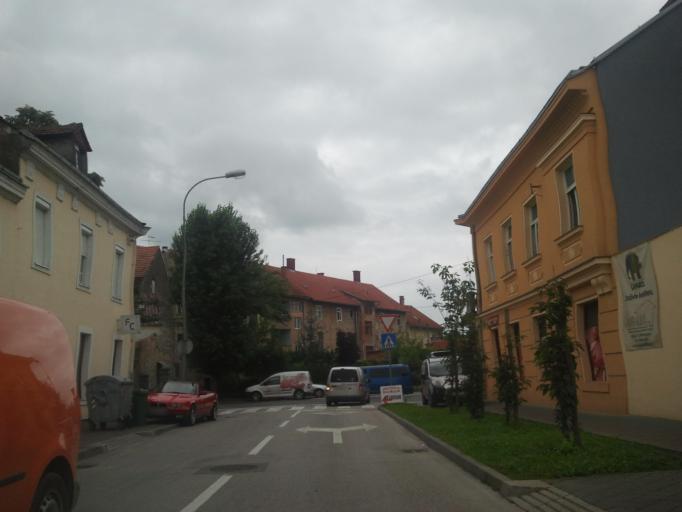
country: HR
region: Karlovacka
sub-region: Grad Karlovac
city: Karlovac
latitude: 45.5012
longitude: 15.5503
